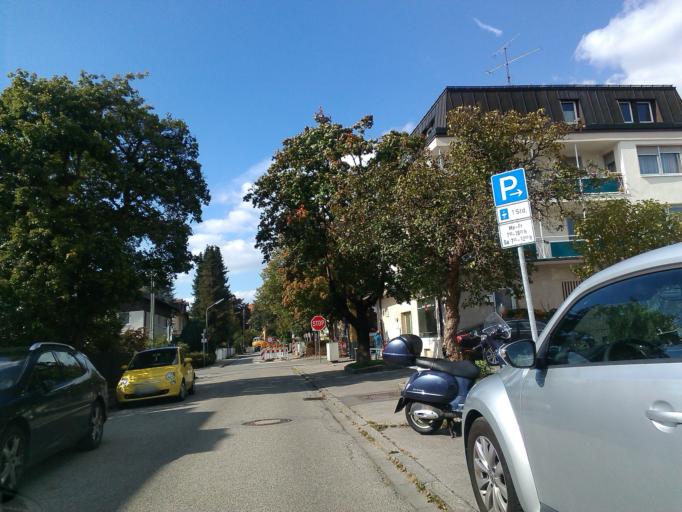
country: DE
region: Bavaria
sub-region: Upper Bavaria
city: Planegg
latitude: 48.1004
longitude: 11.4154
